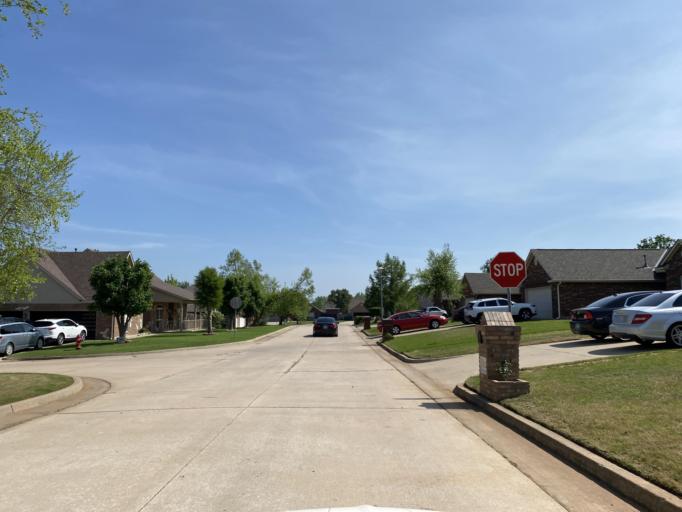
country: US
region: Oklahoma
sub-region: Oklahoma County
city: Nicoma Park
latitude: 35.4726
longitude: -97.3397
